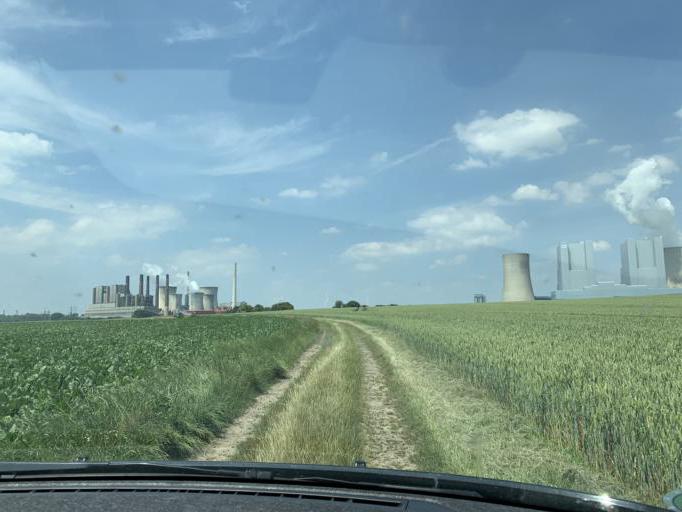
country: DE
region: North Rhine-Westphalia
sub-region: Regierungsbezirk Dusseldorf
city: Rommerskirchen
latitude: 51.0236
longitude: 6.6286
